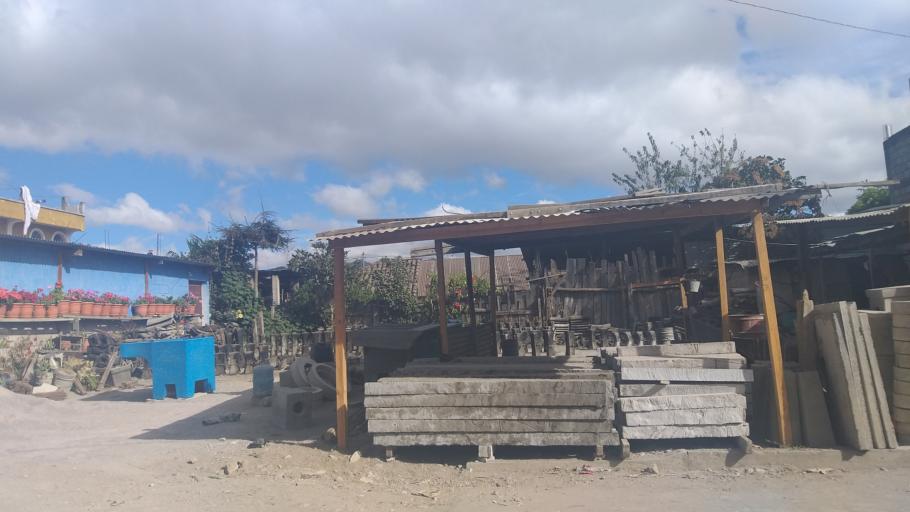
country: GT
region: Quetzaltenango
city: Ostuncalco
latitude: 14.8684
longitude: -91.6248
